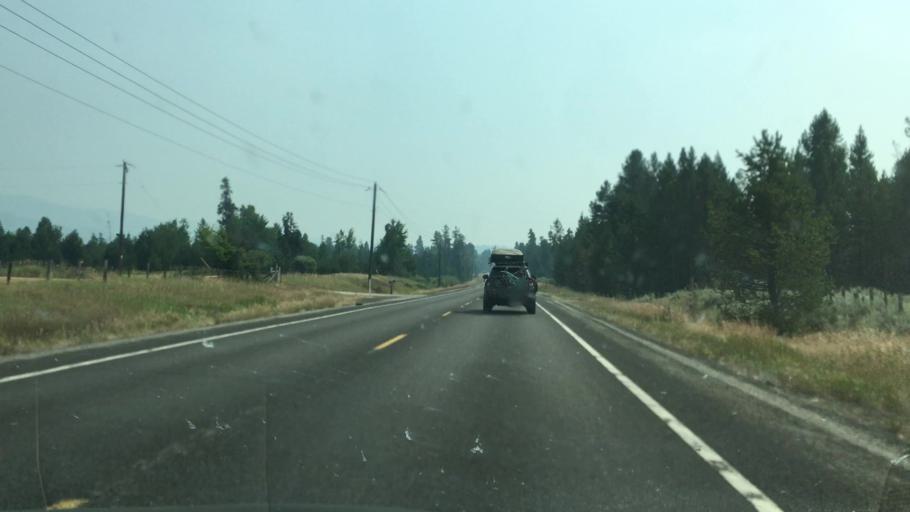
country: US
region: Idaho
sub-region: Valley County
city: Cascade
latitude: 44.4147
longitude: -115.9998
